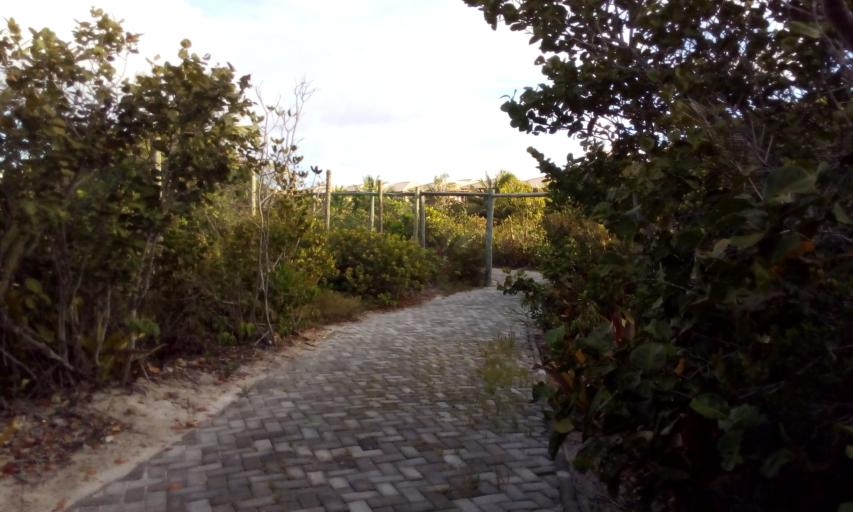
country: BR
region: Bahia
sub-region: Mata De Sao Joao
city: Mata de Sao Joao
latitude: -12.5694
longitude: -38.0035
